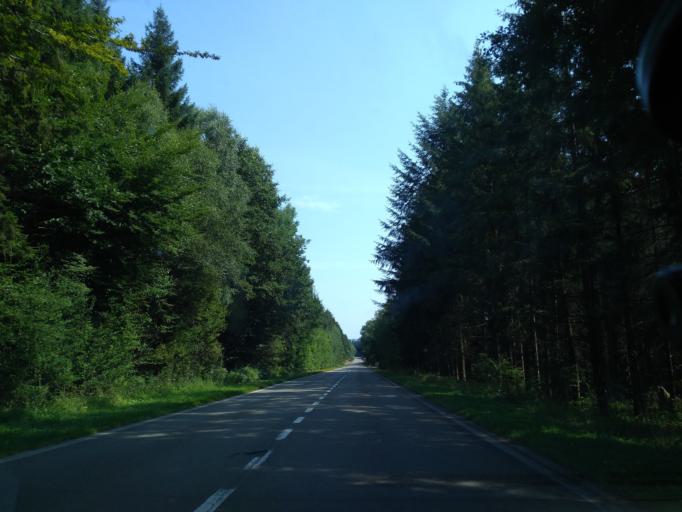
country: BE
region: Wallonia
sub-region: Province du Luxembourg
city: Tenneville
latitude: 50.1348
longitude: 5.4913
